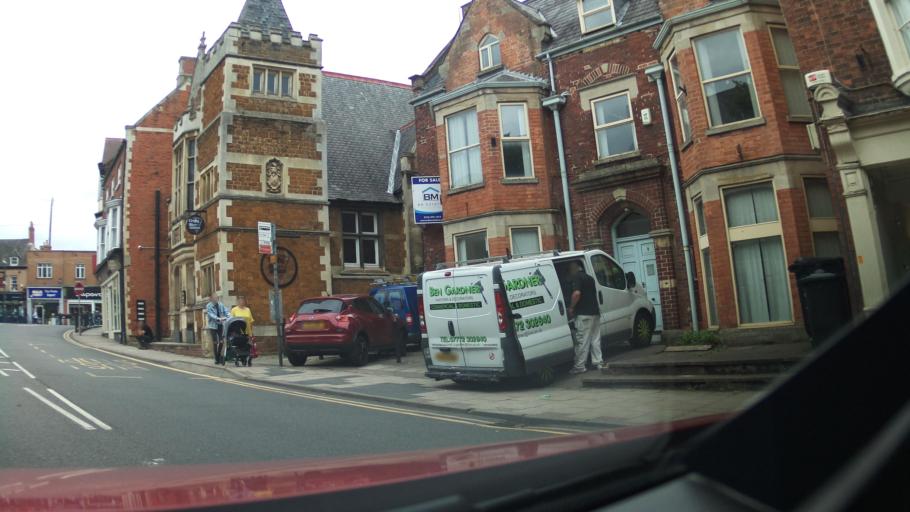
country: GB
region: England
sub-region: Leicestershire
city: Melton Mowbray
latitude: 52.7639
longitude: -0.8854
